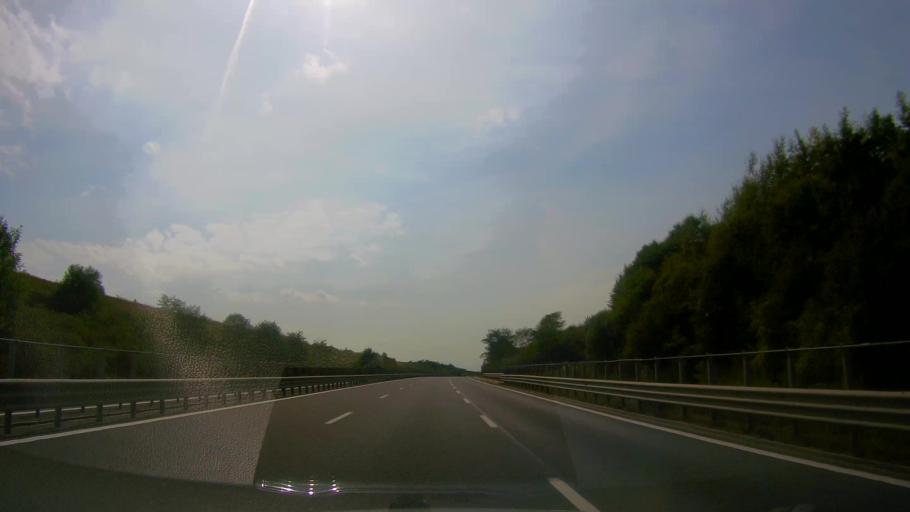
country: RO
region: Cluj
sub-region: Comuna Floresti
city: Luna de Sus
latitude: 46.7459
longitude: 23.4179
